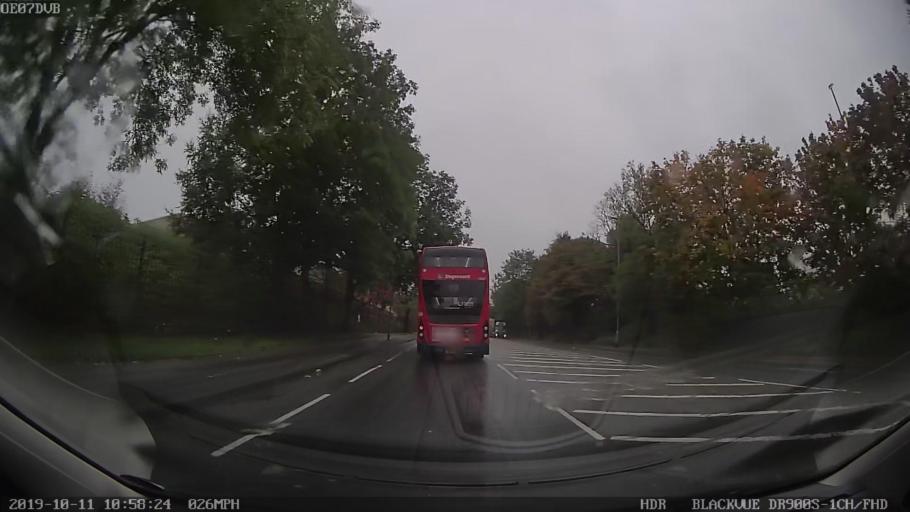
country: GB
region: England
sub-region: Borough of Rochdale
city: Middleton
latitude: 53.5382
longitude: -2.1753
